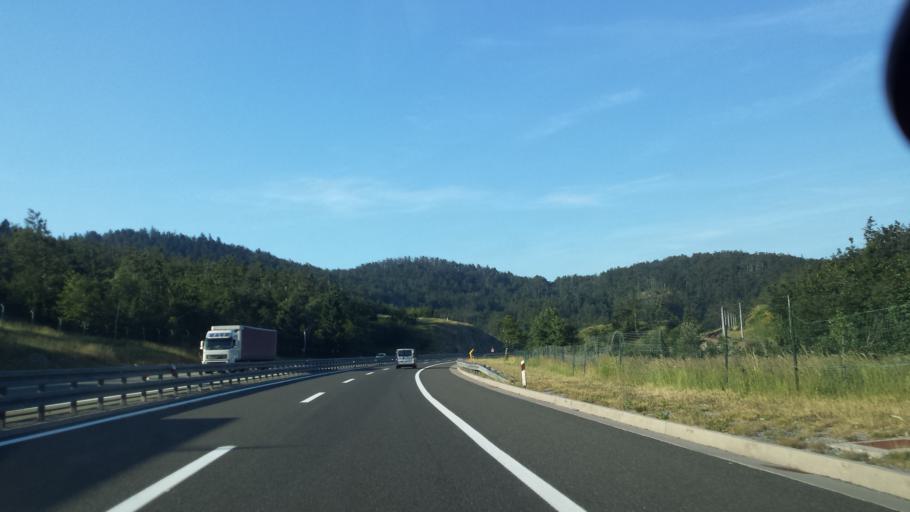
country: HR
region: Primorsko-Goranska
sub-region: Grad Delnice
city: Delnice
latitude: 45.3346
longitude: 14.7386
